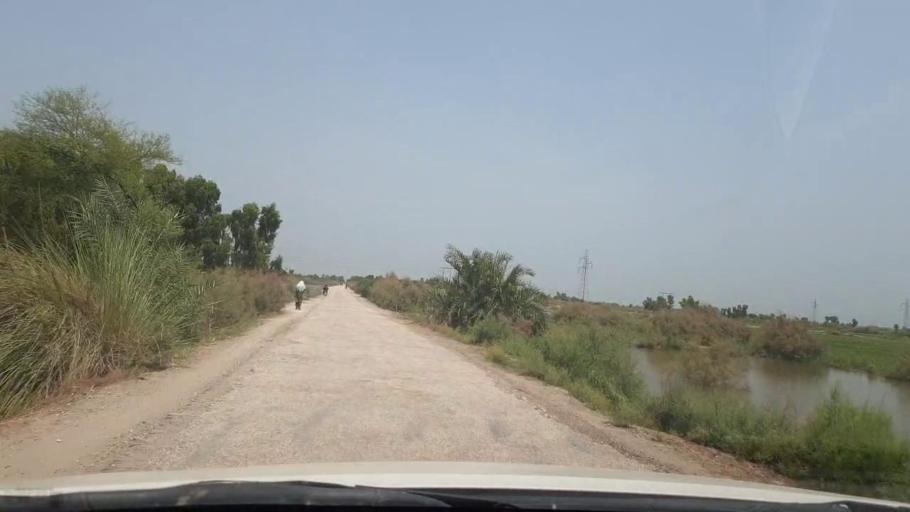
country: PK
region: Sindh
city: Rustam jo Goth
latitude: 28.0248
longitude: 68.8128
